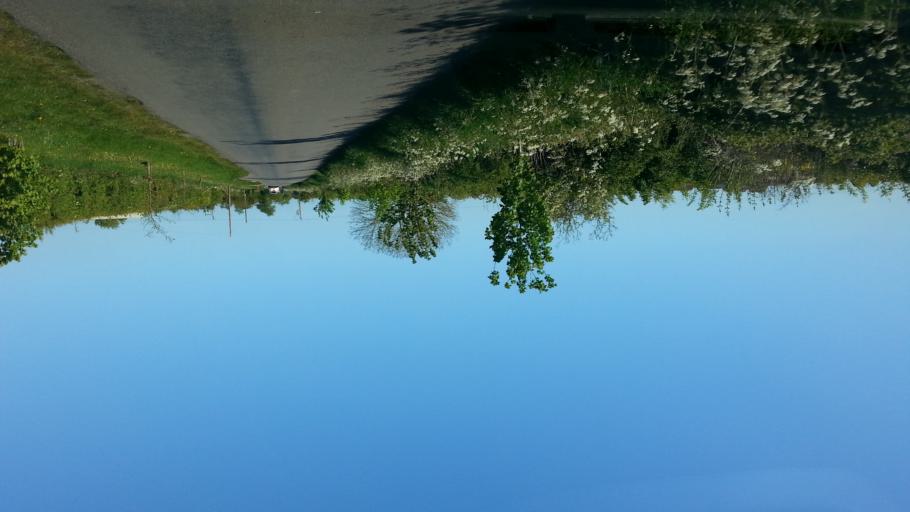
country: GB
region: England
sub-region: Lincolnshire
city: Long Bennington
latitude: 53.0263
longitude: -0.7328
